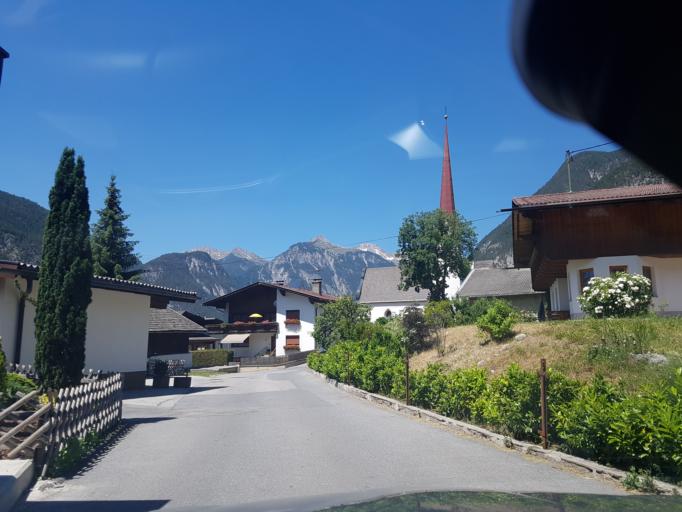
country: AT
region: Tyrol
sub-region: Politischer Bezirk Imst
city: Nassereith
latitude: 47.3072
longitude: 10.8524
